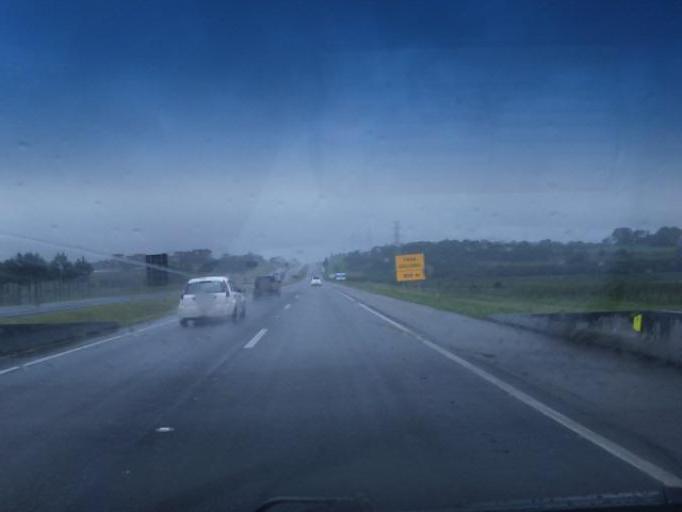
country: BR
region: Parana
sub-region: Piraquara
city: Piraquara
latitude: -25.5045
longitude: -49.1228
